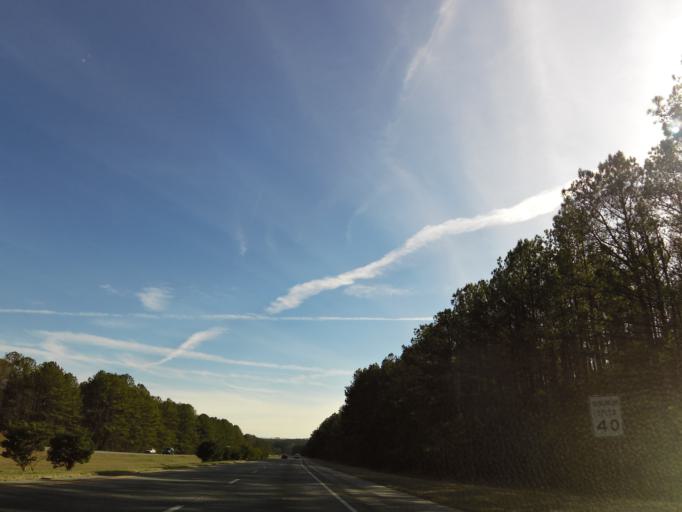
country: US
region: Georgia
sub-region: Harris County
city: Hamilton
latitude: 32.6494
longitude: -84.9724
